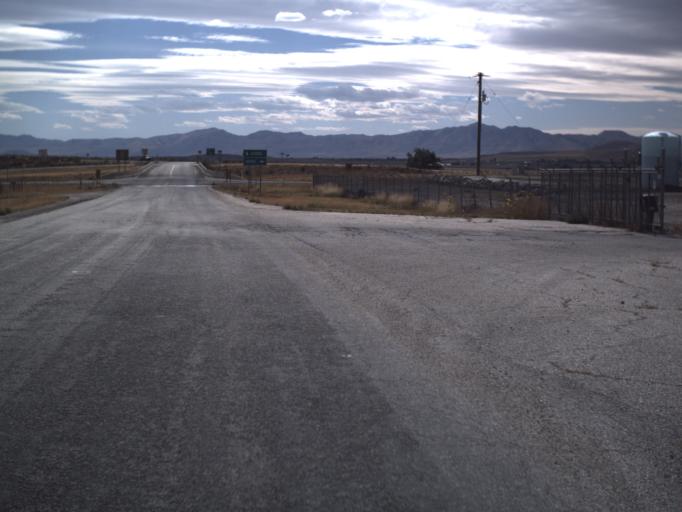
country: US
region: Utah
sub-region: Box Elder County
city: Tremonton
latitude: 41.7224
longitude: -112.2270
